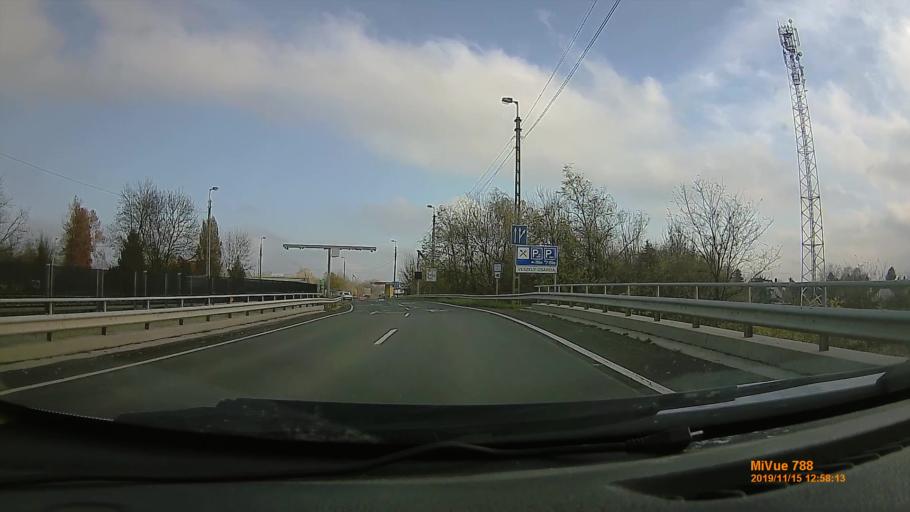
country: HU
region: Bekes
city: Bekescsaba
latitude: 46.6721
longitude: 21.1750
